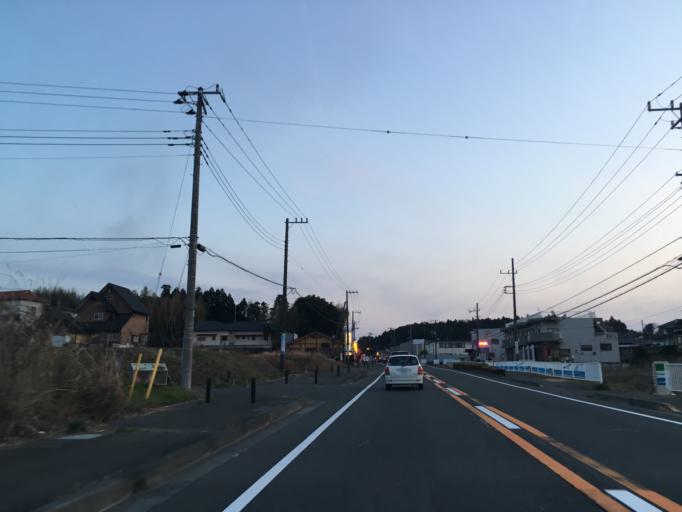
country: JP
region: Ibaraki
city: Takahagi
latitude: 36.7417
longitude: 140.7256
